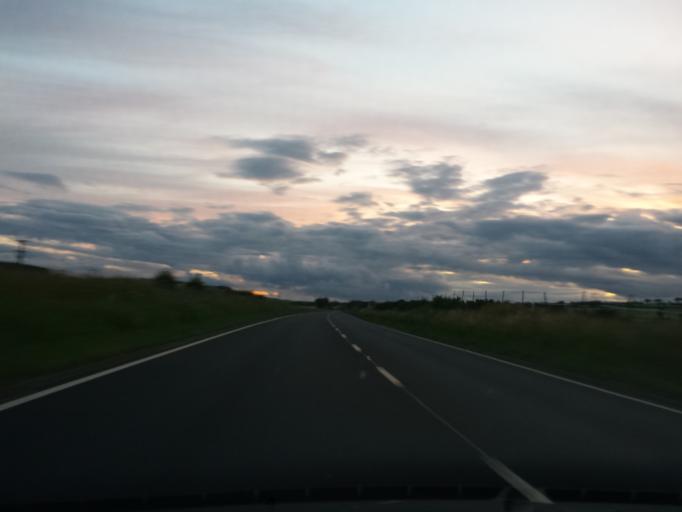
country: GB
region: Scotland
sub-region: The Scottish Borders
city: Chirnside
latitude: 55.8558
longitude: -2.1997
